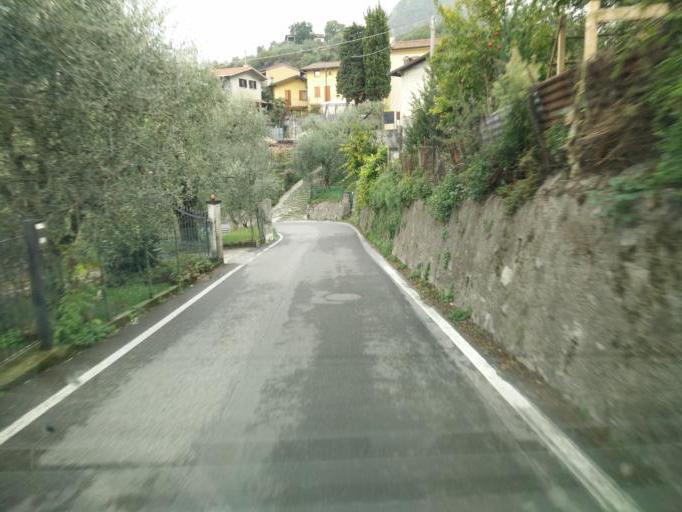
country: IT
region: Lombardy
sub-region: Provincia di Brescia
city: Marone
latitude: 45.7373
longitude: 10.1009
